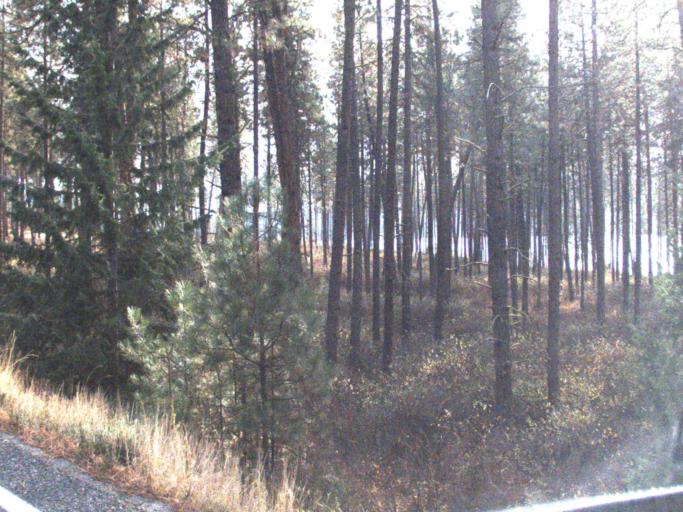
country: US
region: Washington
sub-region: Stevens County
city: Kettle Falls
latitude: 48.2942
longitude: -118.1435
